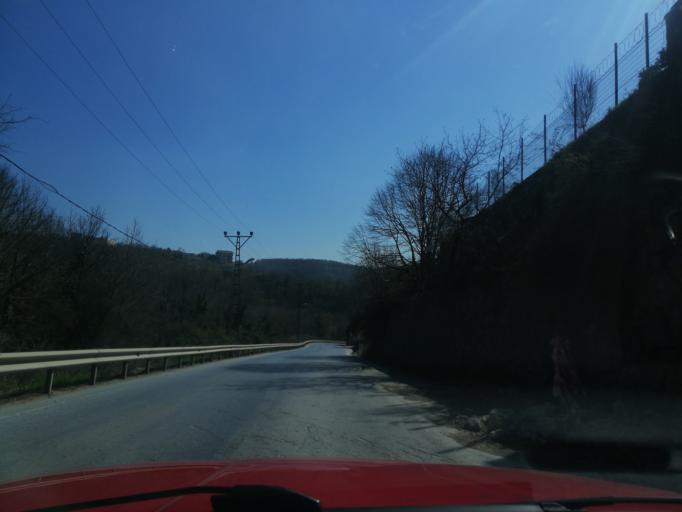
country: TR
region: Istanbul
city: Mahmut Sevket Pasa
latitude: 41.1022
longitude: 29.1587
